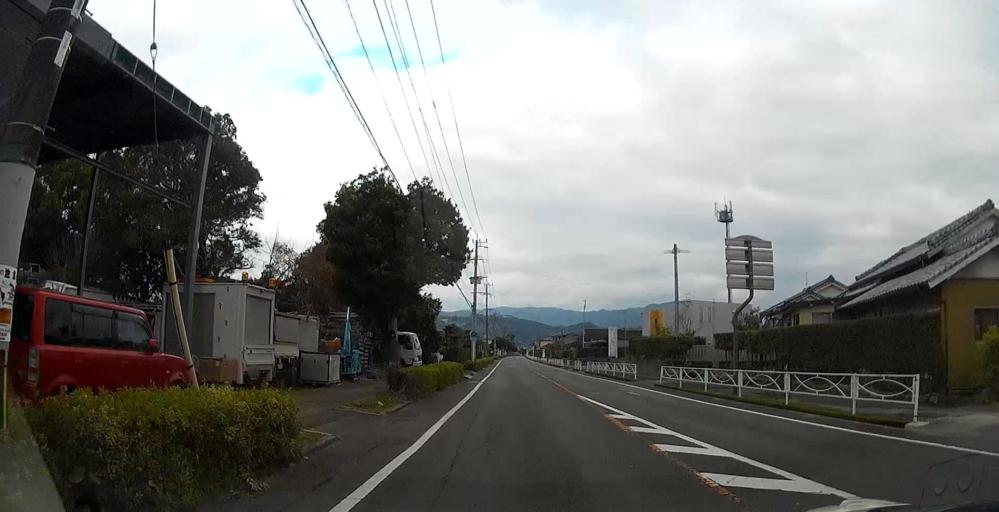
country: JP
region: Kagoshima
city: Izumi
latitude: 32.0748
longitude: 130.3486
